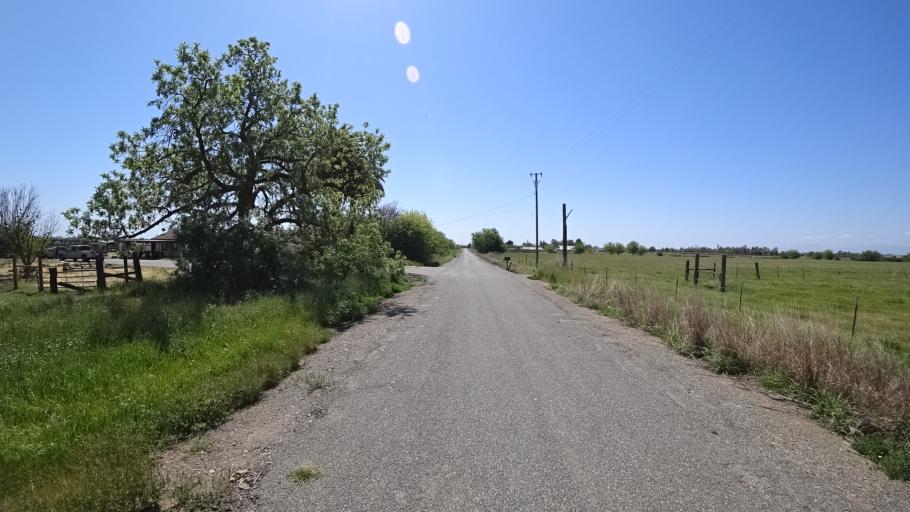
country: US
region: California
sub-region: Glenn County
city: Orland
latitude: 39.7782
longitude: -122.1830
